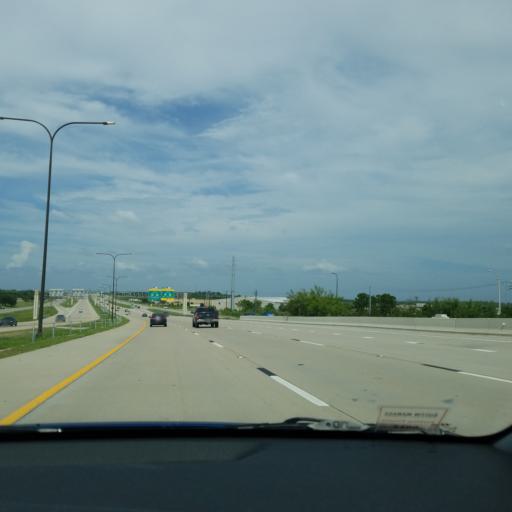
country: US
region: Texas
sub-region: Travis County
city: Manor
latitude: 30.3308
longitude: -97.6223
